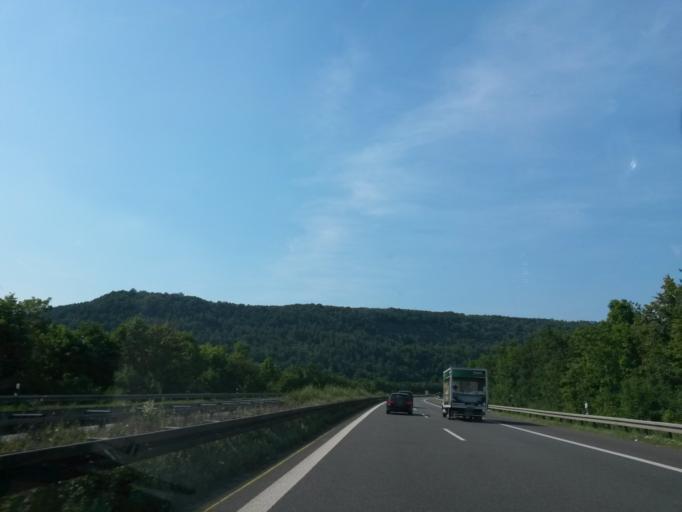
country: DE
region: Bavaria
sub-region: Regierungsbezirk Unterfranken
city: Elfershausen
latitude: 50.1365
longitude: 9.9520
